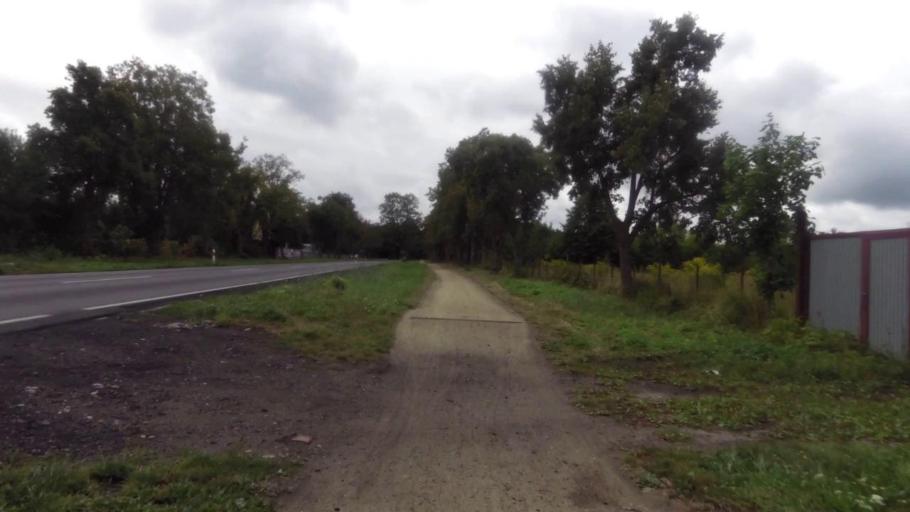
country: PL
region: West Pomeranian Voivodeship
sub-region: Powiat mysliborski
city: Debno
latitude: 52.7248
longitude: 14.6937
